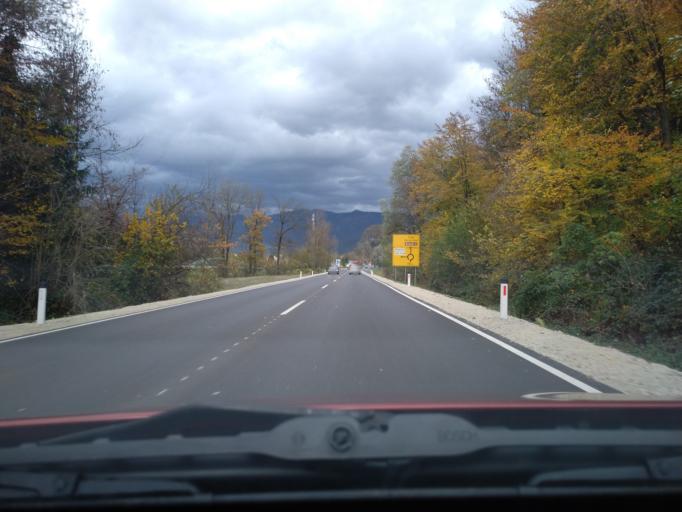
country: SI
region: Kamnik
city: Smarca
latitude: 46.2039
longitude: 14.6032
